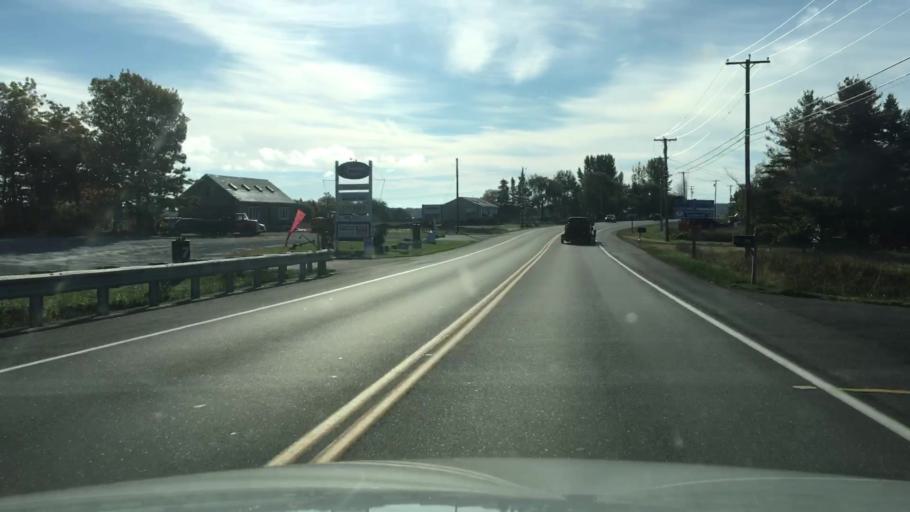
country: US
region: Maine
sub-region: Knox County
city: Warren
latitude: 44.0839
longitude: -69.2279
